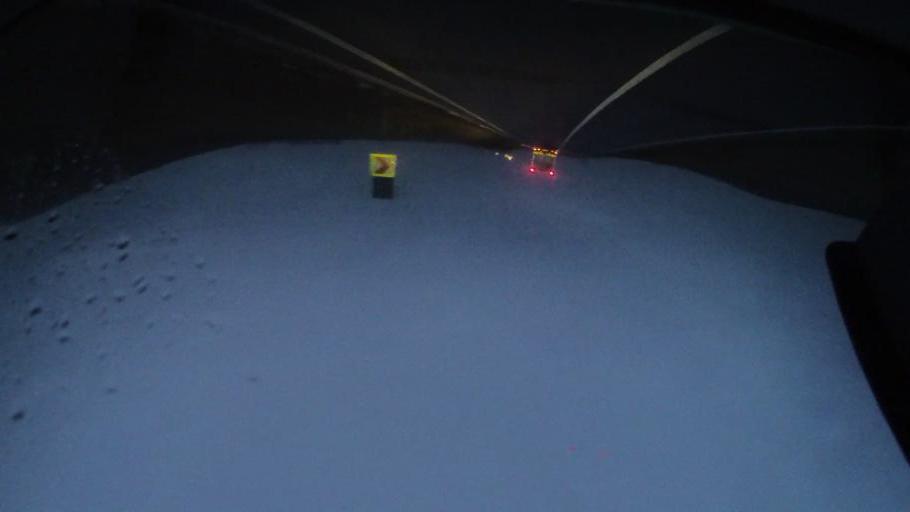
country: RO
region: Harghita
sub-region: Comuna Subcetate
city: Subcetate
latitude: 46.8451
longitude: 25.4716
